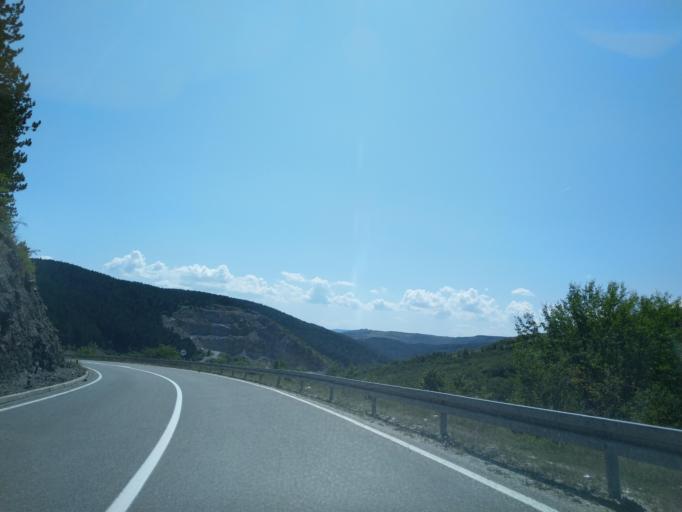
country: RS
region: Central Serbia
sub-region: Zlatiborski Okrug
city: Sjenica
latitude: 43.3016
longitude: 19.9304
